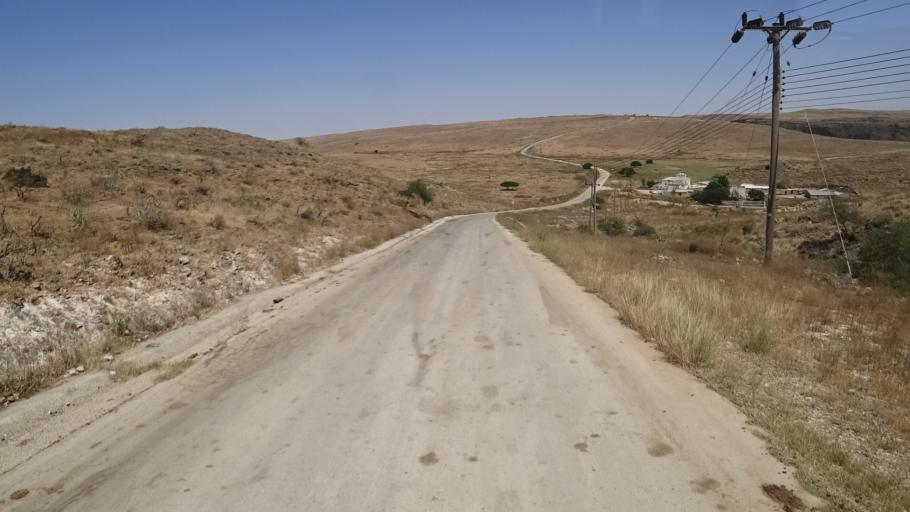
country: OM
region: Zufar
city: Salalah
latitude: 17.1490
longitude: 54.6176
